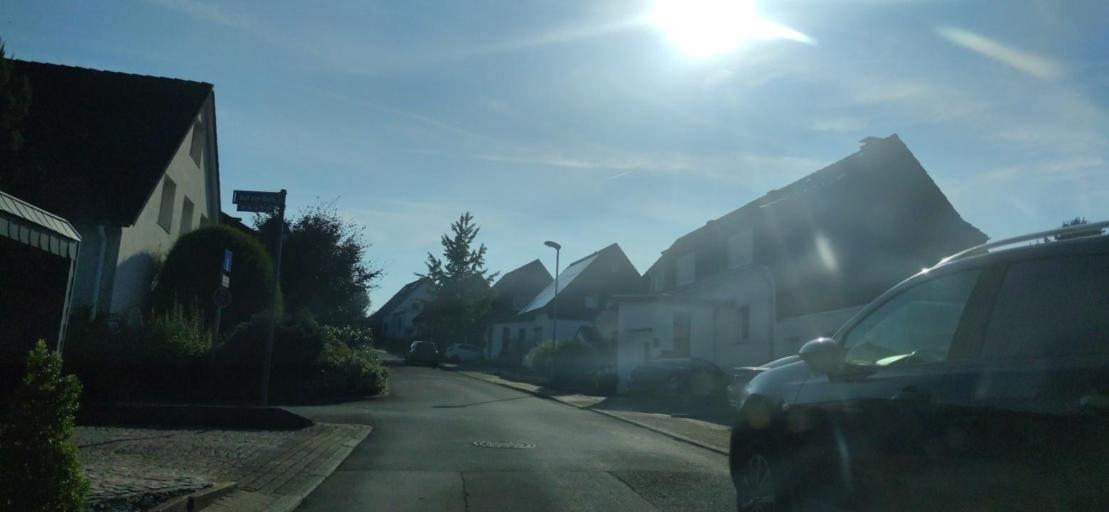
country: DE
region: North Rhine-Westphalia
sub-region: Regierungsbezirk Dusseldorf
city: Essen
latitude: 51.4752
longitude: 7.0623
